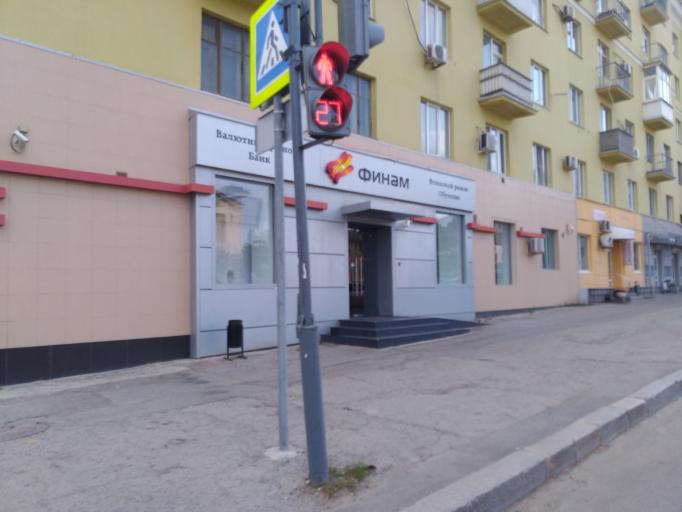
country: RU
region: Volgograd
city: Volgograd
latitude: 48.7161
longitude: 44.5284
